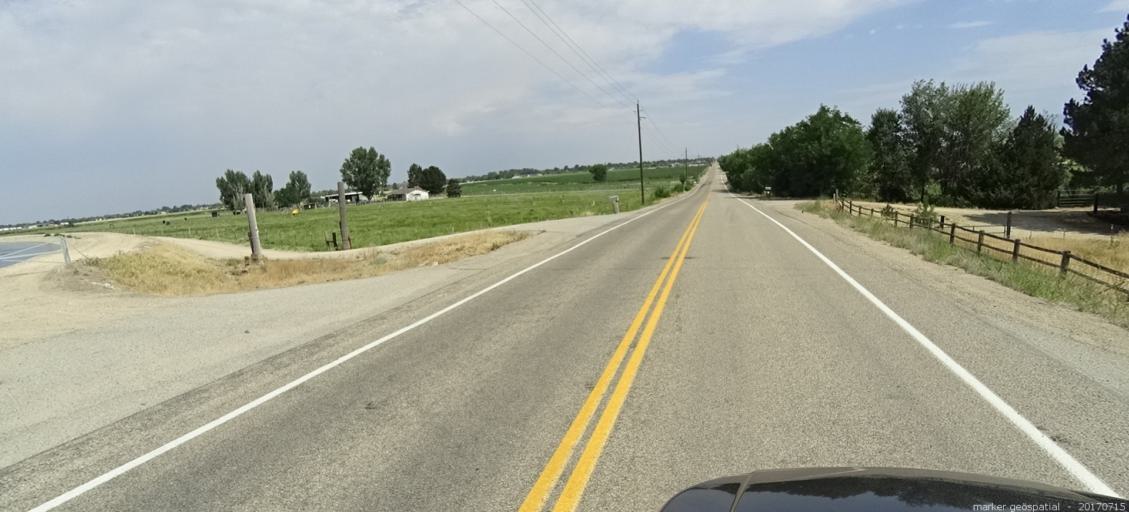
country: US
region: Idaho
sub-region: Ada County
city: Garden City
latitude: 43.5297
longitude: -116.2742
